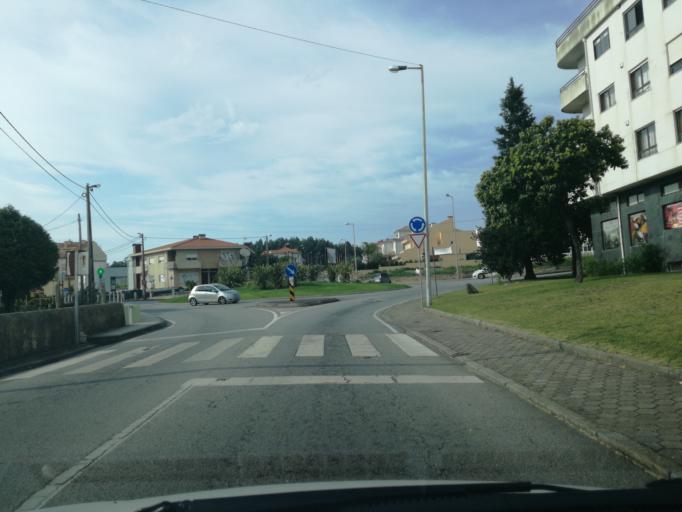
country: PT
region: Porto
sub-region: Vila Nova de Gaia
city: Sao Felix da Marinha
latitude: 41.0243
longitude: -8.6296
